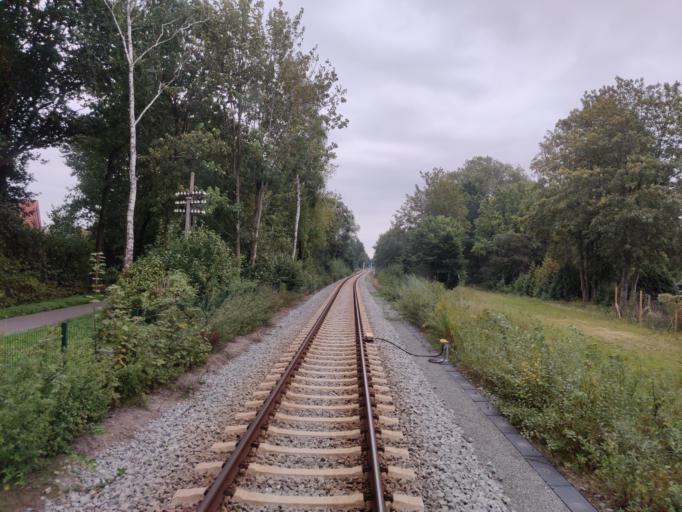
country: DE
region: Lower Saxony
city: Bremervorde
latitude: 53.4811
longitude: 9.1461
